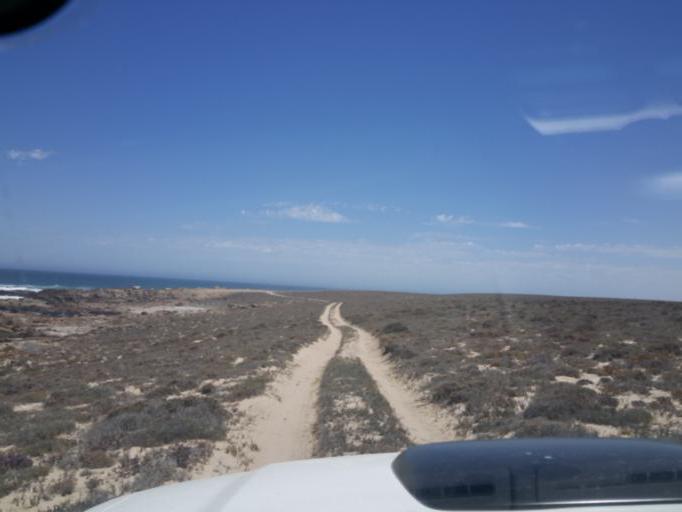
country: ZA
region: Northern Cape
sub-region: Namakwa District Municipality
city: Garies
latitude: -30.5660
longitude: 17.4169
